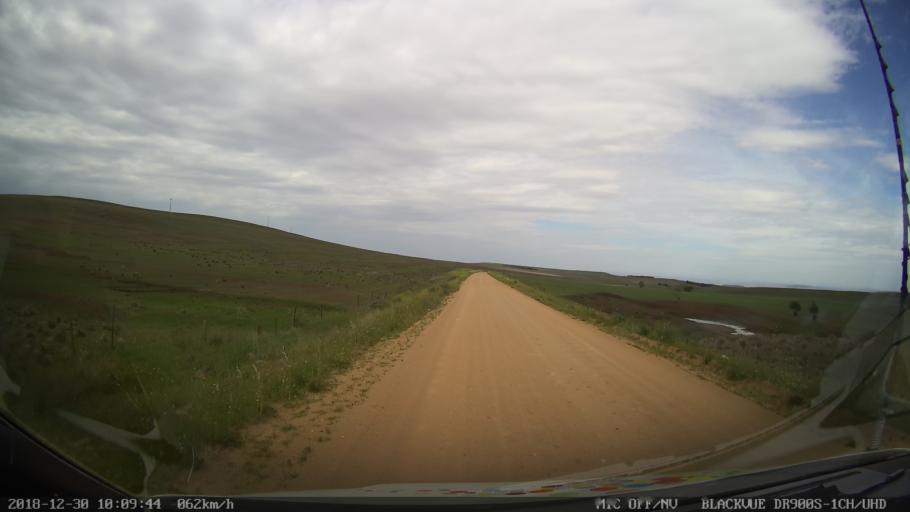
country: AU
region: New South Wales
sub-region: Cooma-Monaro
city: Cooma
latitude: -36.5492
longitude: 149.1023
